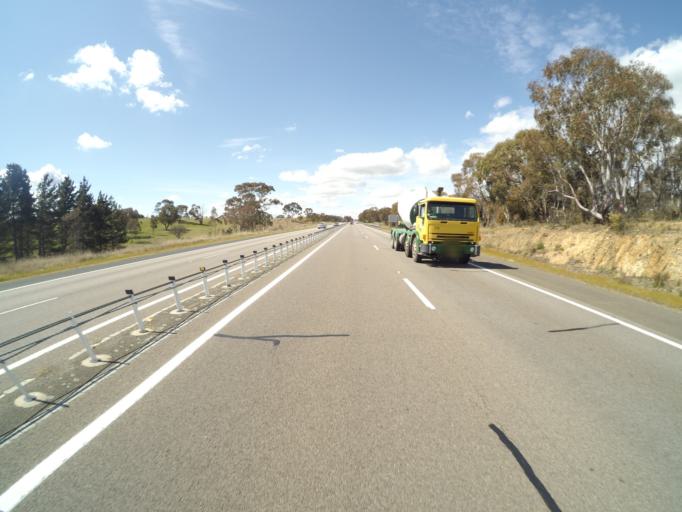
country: AU
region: New South Wales
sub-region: Goulburn Mulwaree
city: Goulburn
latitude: -34.7318
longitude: 149.8126
